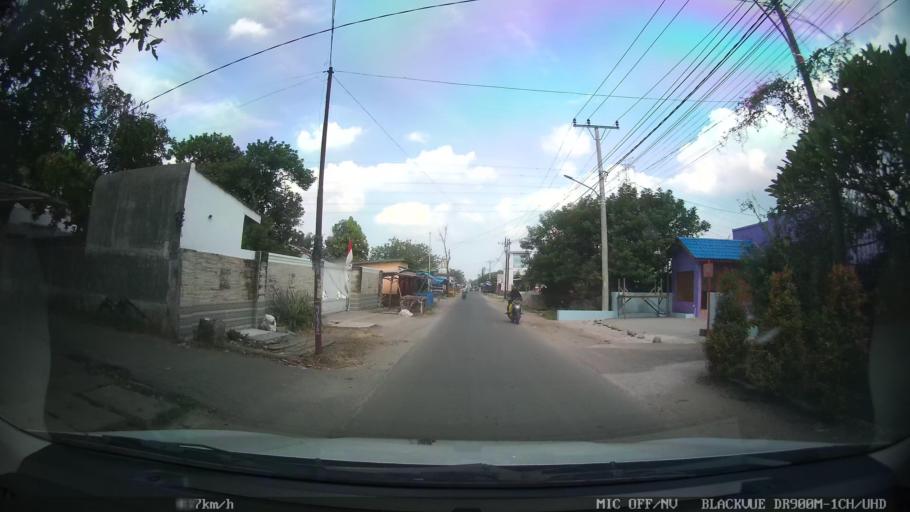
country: ID
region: North Sumatra
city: Binjai
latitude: 3.6132
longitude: 98.5206
